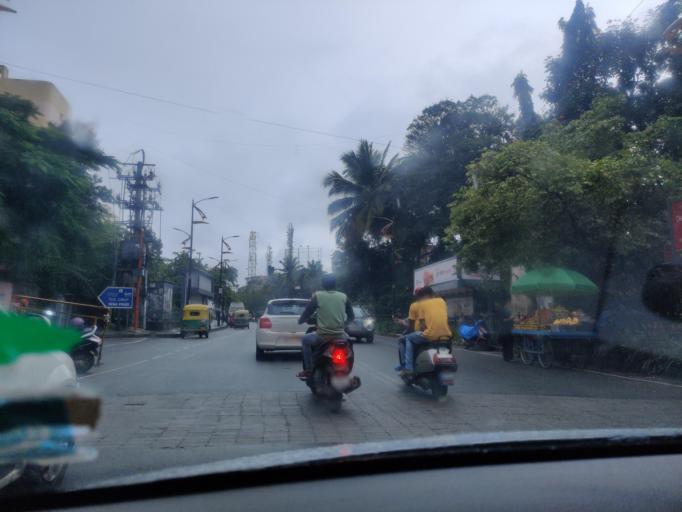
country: IN
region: Karnataka
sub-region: Bangalore Urban
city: Bangalore
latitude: 13.0214
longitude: 77.6371
